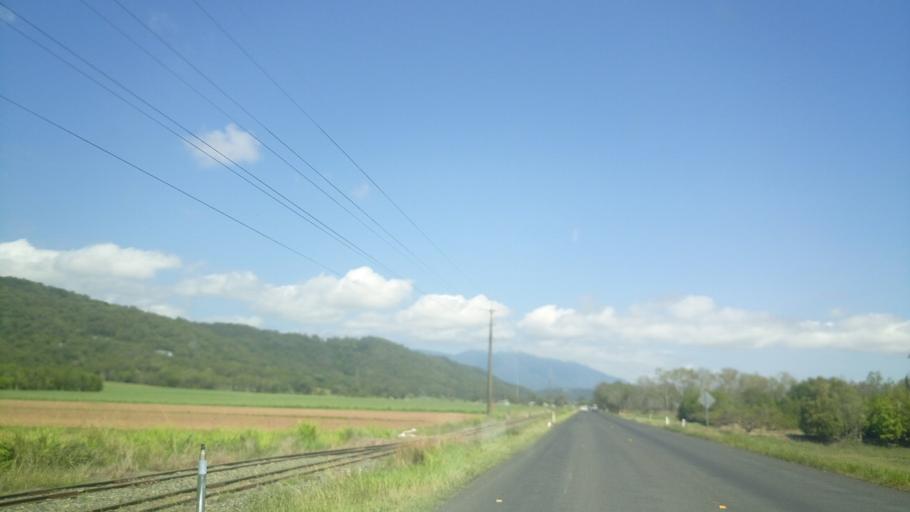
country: AU
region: Queensland
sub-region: Cairns
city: Port Douglas
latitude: -16.5014
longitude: 145.4342
